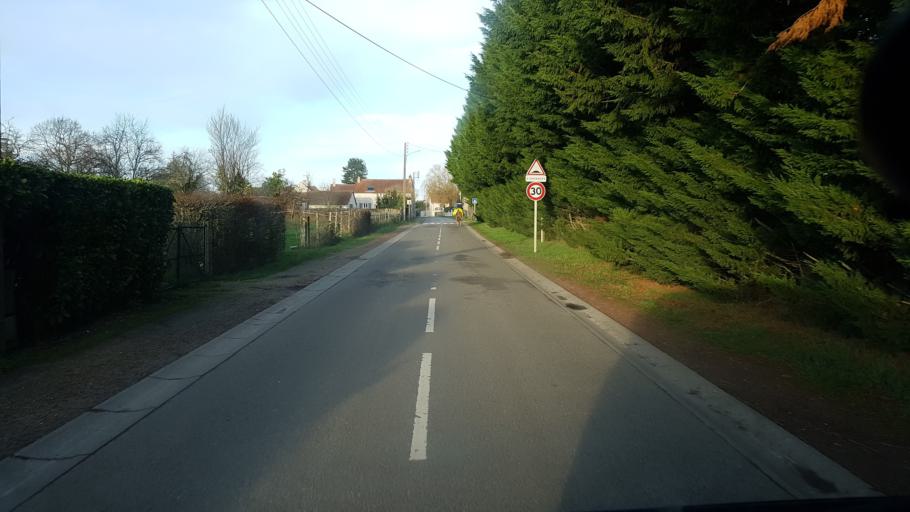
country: FR
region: Ile-de-France
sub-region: Departement des Yvelines
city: Le Perray-en-Yvelines
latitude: 48.7020
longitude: 1.8103
